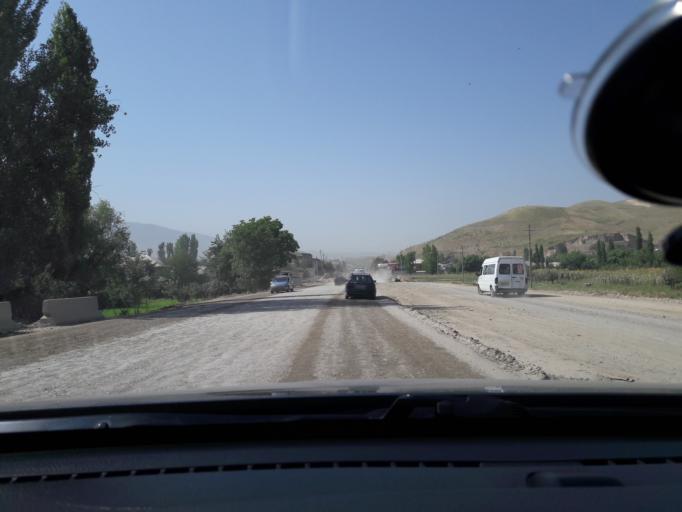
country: TJ
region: Dushanbe
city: Boshkengash
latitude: 38.4480
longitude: 68.7339
